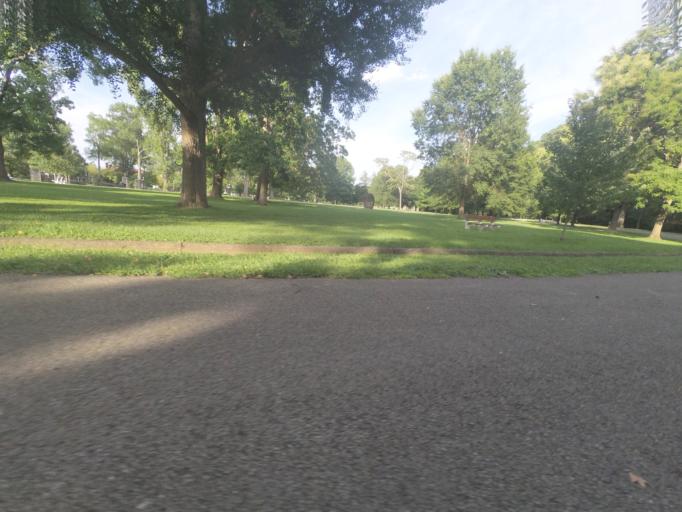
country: US
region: West Virginia
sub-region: Cabell County
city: Huntington
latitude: 38.4075
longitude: -82.4392
